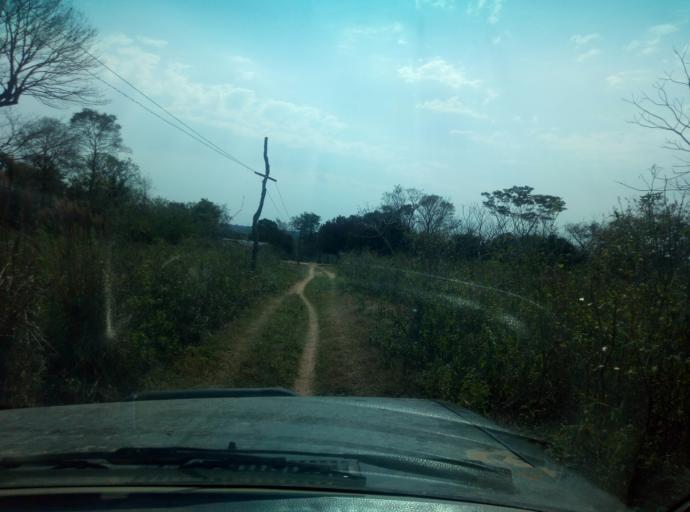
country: PY
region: Caaguazu
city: Doctor Cecilio Baez
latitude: -25.1358
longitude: -56.2430
